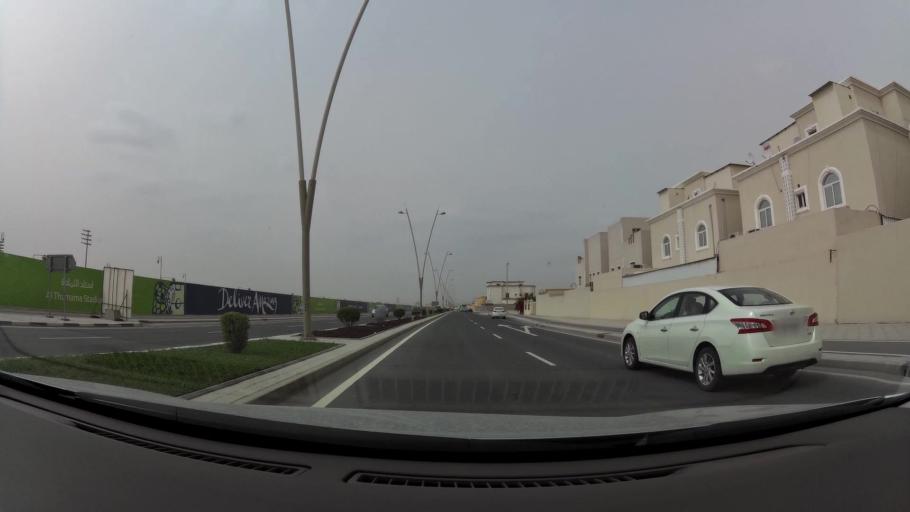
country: QA
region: Baladiyat ad Dawhah
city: Doha
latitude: 25.2323
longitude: 51.5345
